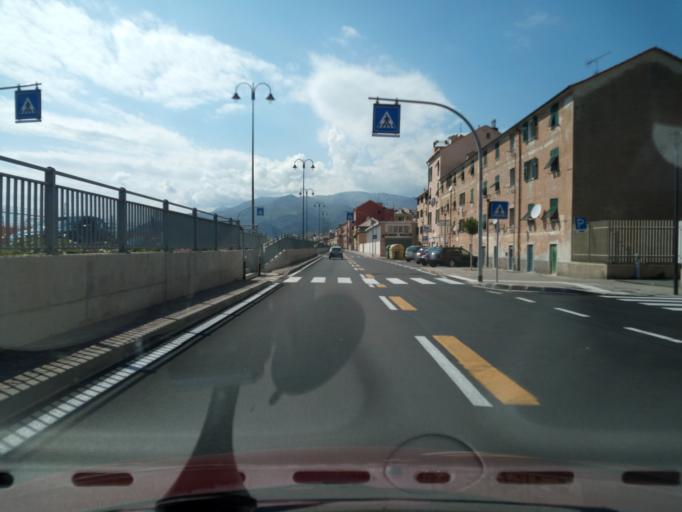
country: IT
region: Liguria
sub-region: Provincia di Genova
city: Mele
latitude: 44.4258
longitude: 8.7937
